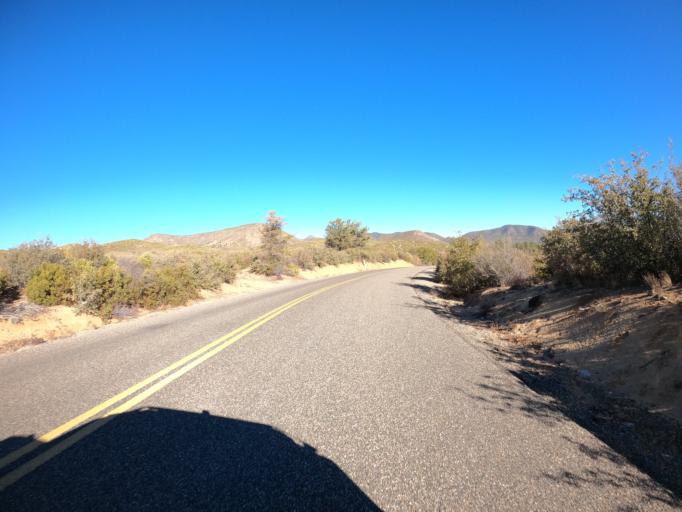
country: US
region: Arizona
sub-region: Yavapai County
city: Verde Village
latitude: 34.5715
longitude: -112.0732
